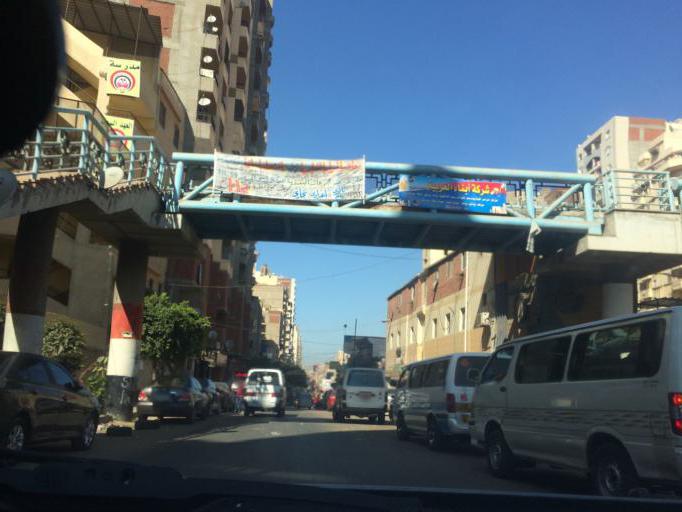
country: EG
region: Alexandria
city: Alexandria
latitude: 31.2493
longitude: 29.9808
